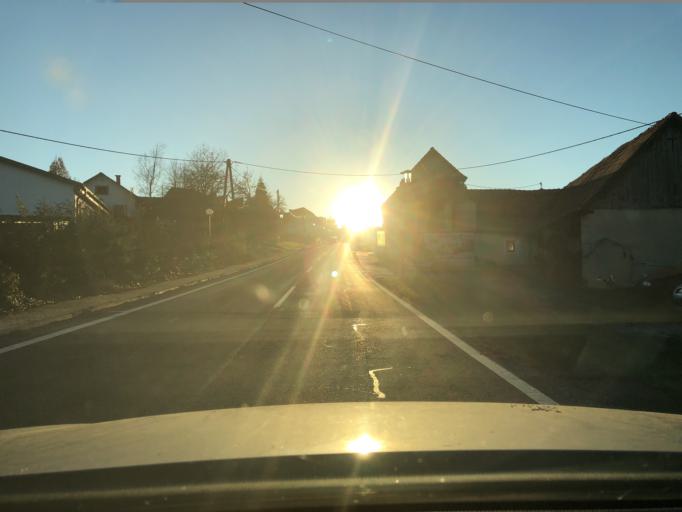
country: AT
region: Styria
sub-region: Politischer Bezirk Weiz
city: Nitscha
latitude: 47.0969
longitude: 15.7607
